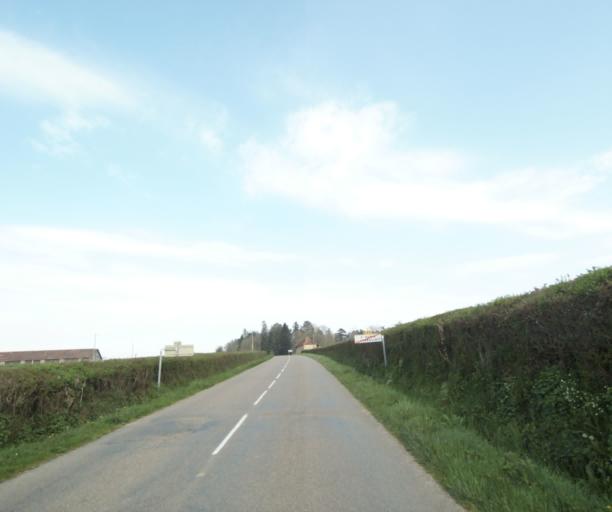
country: FR
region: Bourgogne
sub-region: Departement de Saone-et-Loire
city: Palinges
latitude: 46.4997
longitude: 4.2118
